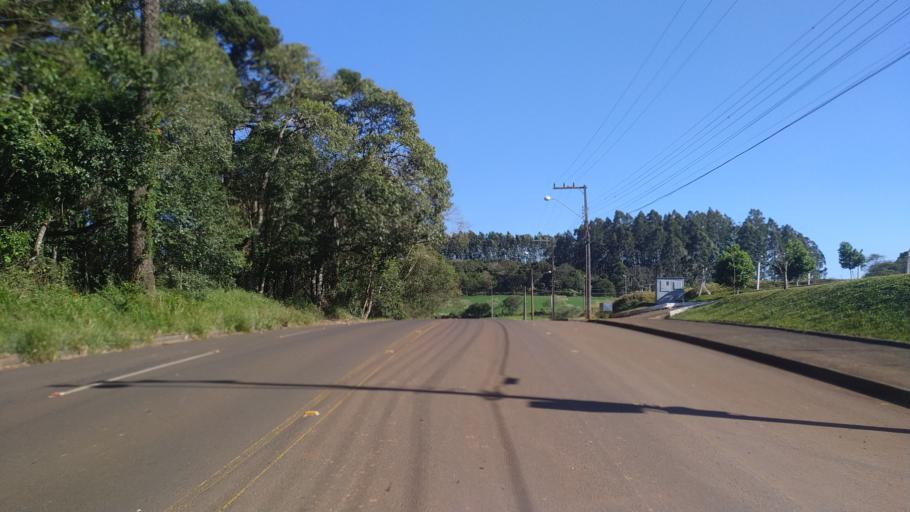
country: BR
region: Santa Catarina
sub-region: Chapeco
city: Chapeco
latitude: -27.1607
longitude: -52.6041
